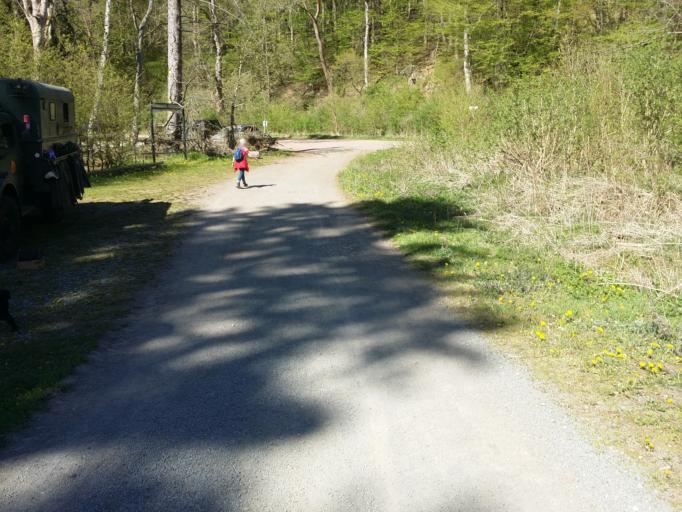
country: DE
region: Saxony-Anhalt
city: Harzgerode
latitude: 51.6738
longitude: 11.1917
